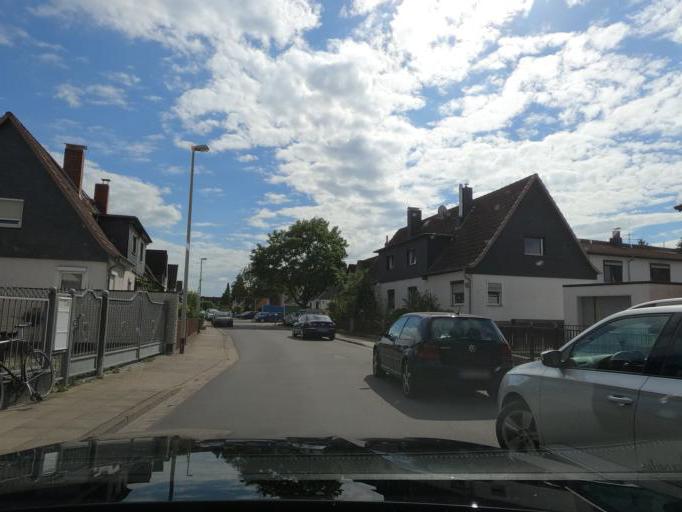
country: DE
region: Lower Saxony
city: Isernhagen Farster Bauerschaft
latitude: 52.3969
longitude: 9.8323
